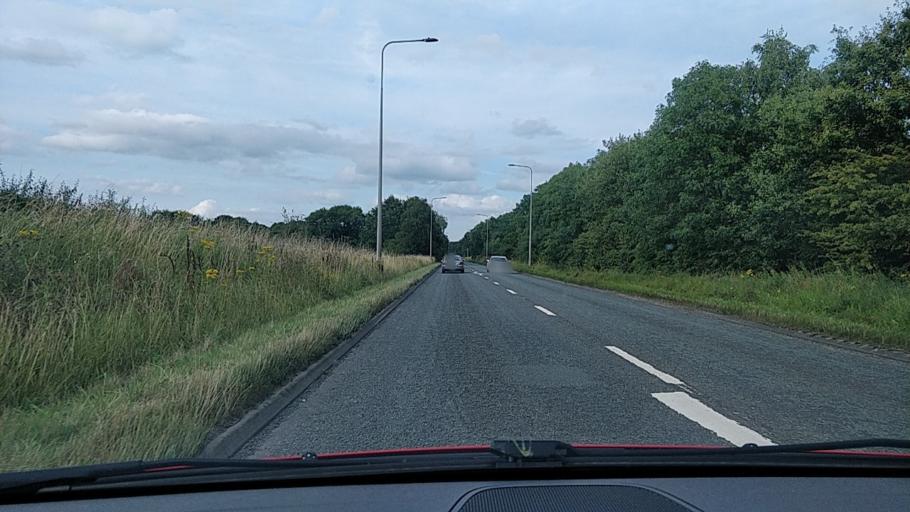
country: GB
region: Wales
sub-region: County of Flintshire
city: Penyffordd
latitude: 53.1483
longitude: -3.0507
